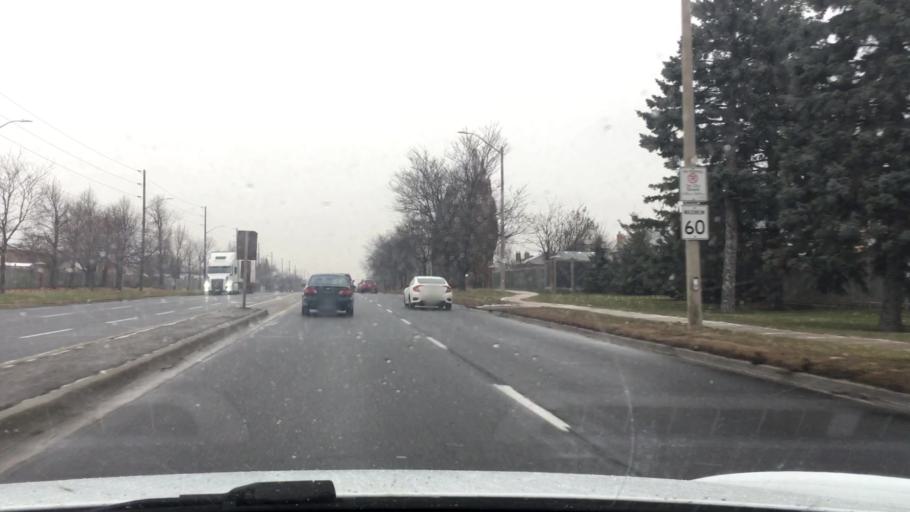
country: CA
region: Ontario
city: Markham
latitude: 43.8421
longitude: -79.2780
